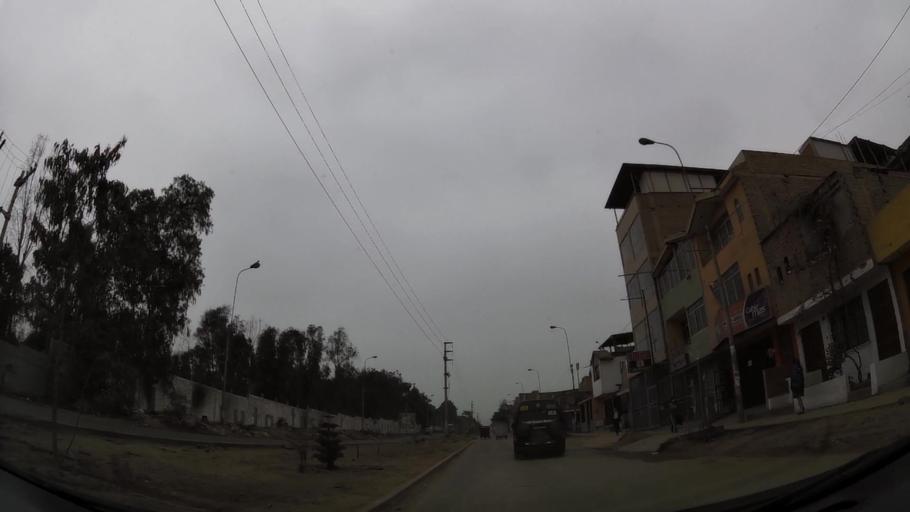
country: PE
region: Lima
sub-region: Lima
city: Surco
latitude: -12.2355
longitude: -76.9234
